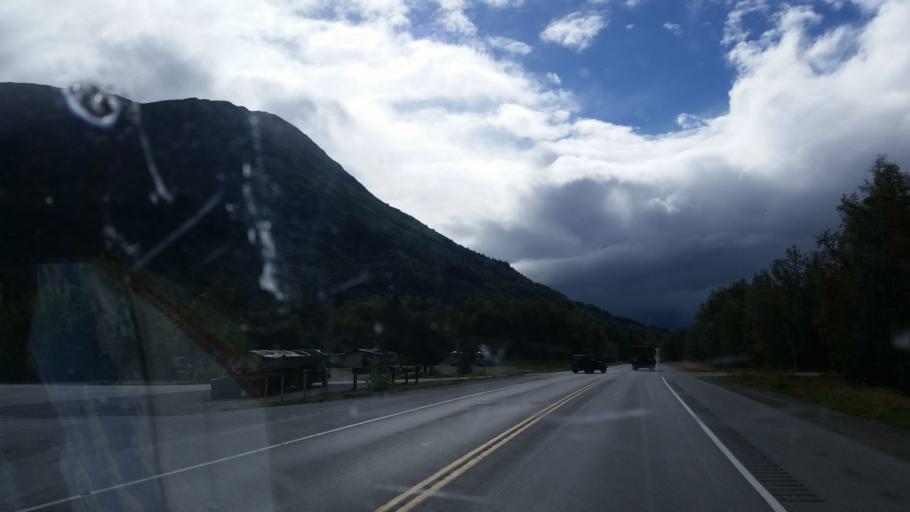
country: US
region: Alaska
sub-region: Anchorage Municipality
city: Girdwood
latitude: 60.9696
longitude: -149.4501
